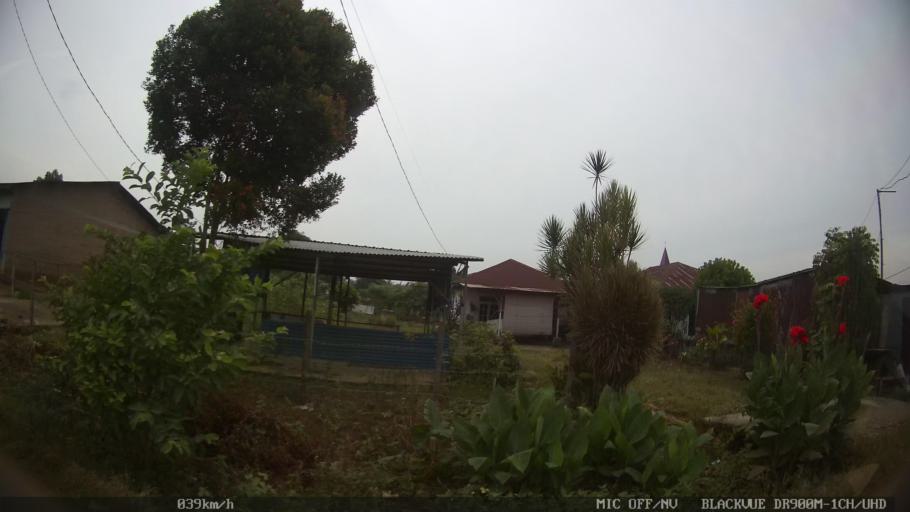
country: ID
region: North Sumatra
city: Deli Tua
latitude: 3.5487
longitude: 98.7280
